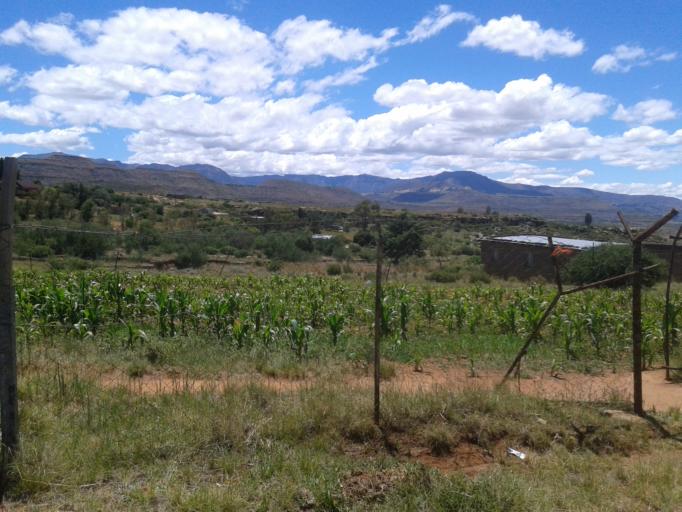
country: LS
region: Quthing
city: Quthing
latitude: -30.3811
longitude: 27.5563
